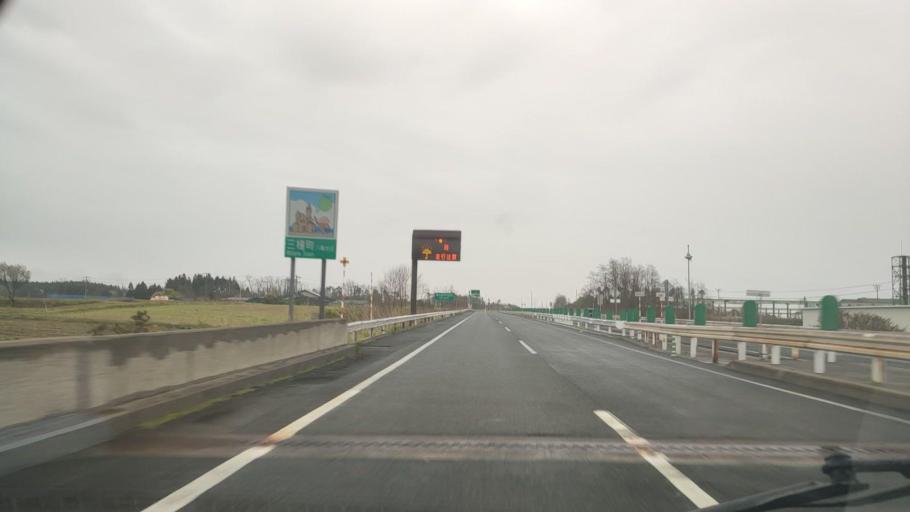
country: JP
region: Akita
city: Noshiromachi
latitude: 40.1246
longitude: 140.0123
